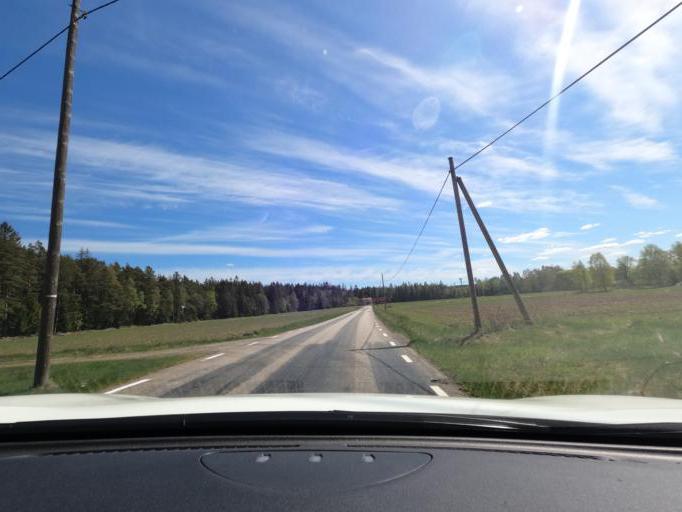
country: SE
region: Vaestra Goetaland
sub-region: Marks Kommun
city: Horred
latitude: 57.4235
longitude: 12.3666
